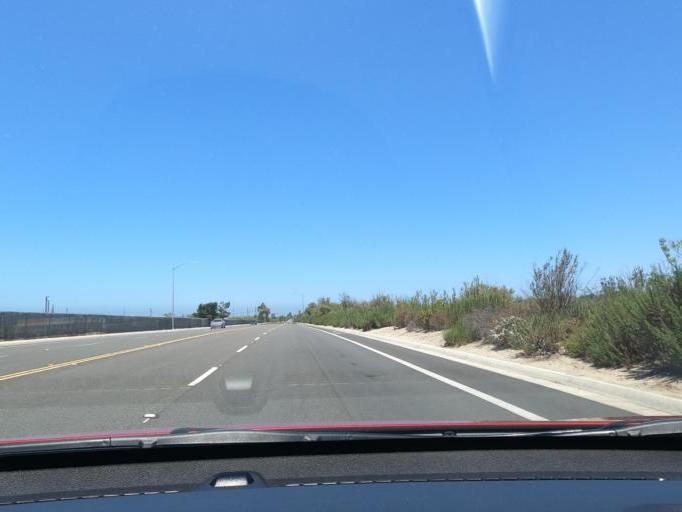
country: US
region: California
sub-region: San Diego County
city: Imperial Beach
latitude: 32.5528
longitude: -117.0582
